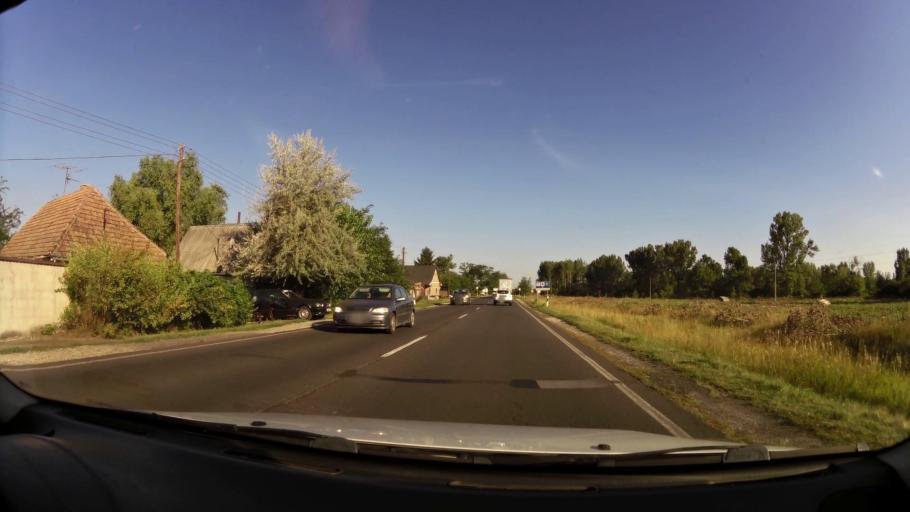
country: HU
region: Pest
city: Pilis
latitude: 47.2751
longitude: 19.5607
